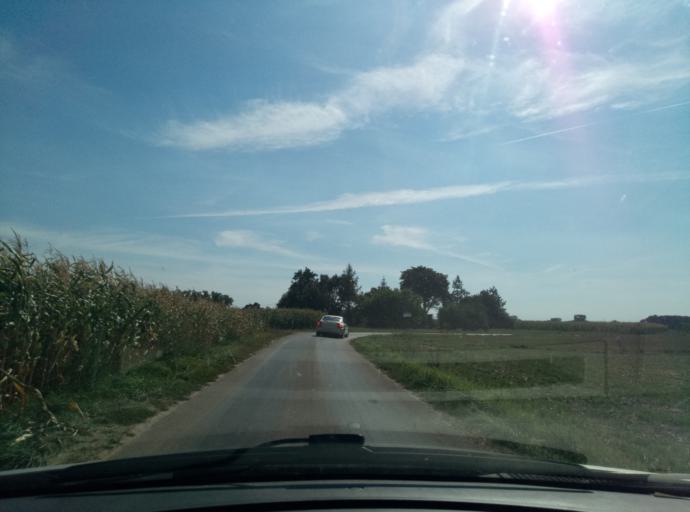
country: PL
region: Kujawsko-Pomorskie
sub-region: Powiat brodnicki
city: Jablonowo Pomorskie
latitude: 53.4053
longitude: 19.2378
